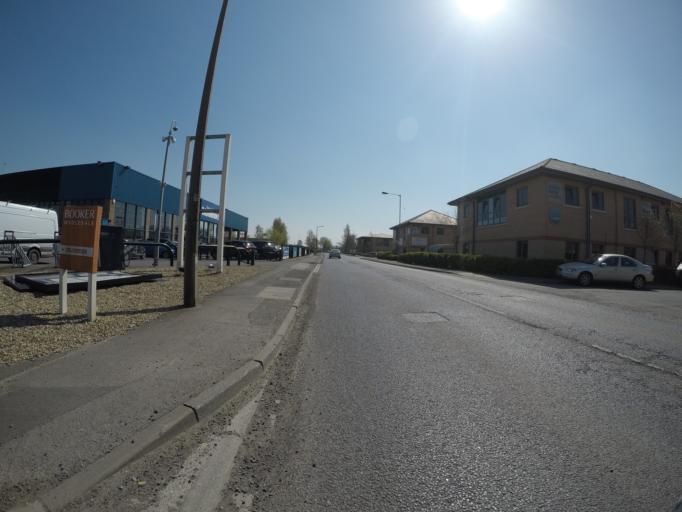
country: GB
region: England
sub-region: City of York
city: Wigginton
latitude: 53.9915
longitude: -1.0962
